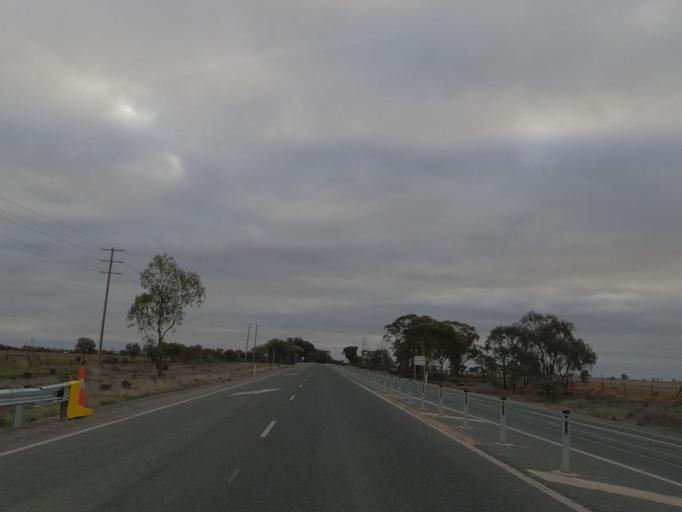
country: AU
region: Victoria
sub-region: Swan Hill
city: Swan Hill
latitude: -35.5501
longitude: 143.7676
